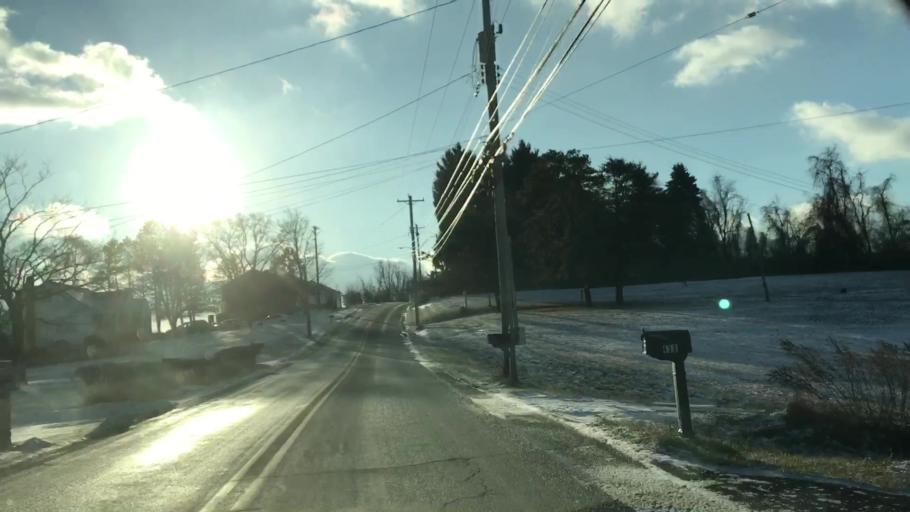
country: US
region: Pennsylvania
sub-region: Allegheny County
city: Enlow
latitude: 40.4759
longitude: -80.1914
